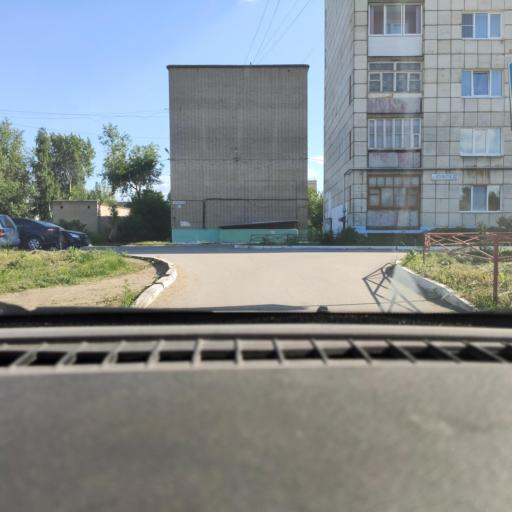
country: RU
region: Perm
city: Krasnokamsk
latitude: 58.0876
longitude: 55.7797
